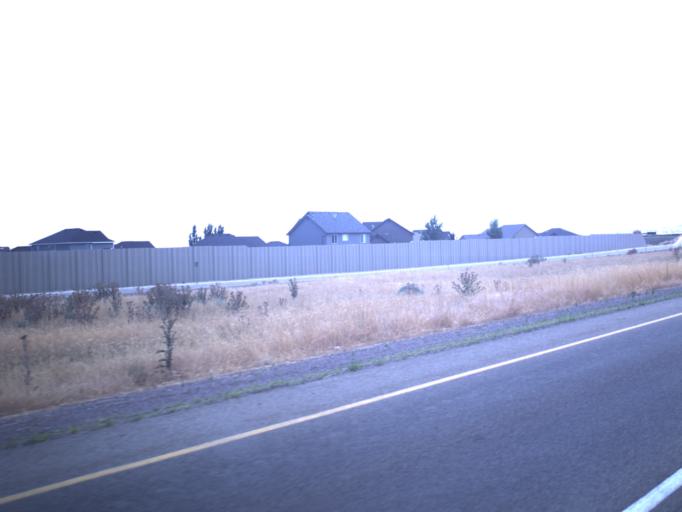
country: US
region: Utah
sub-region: Salt Lake County
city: Herriman
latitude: 40.5178
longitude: -112.0058
